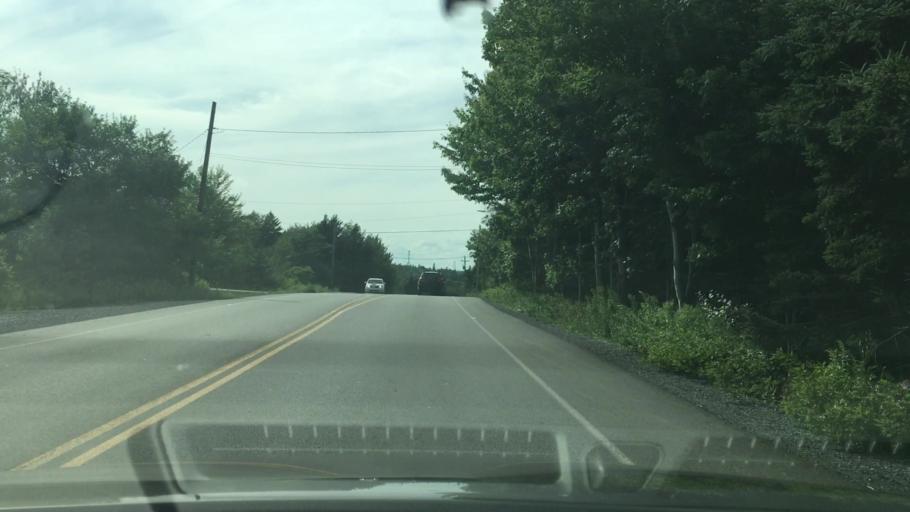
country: CA
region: Nova Scotia
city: Dartmouth
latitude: 44.7262
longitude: -63.7414
